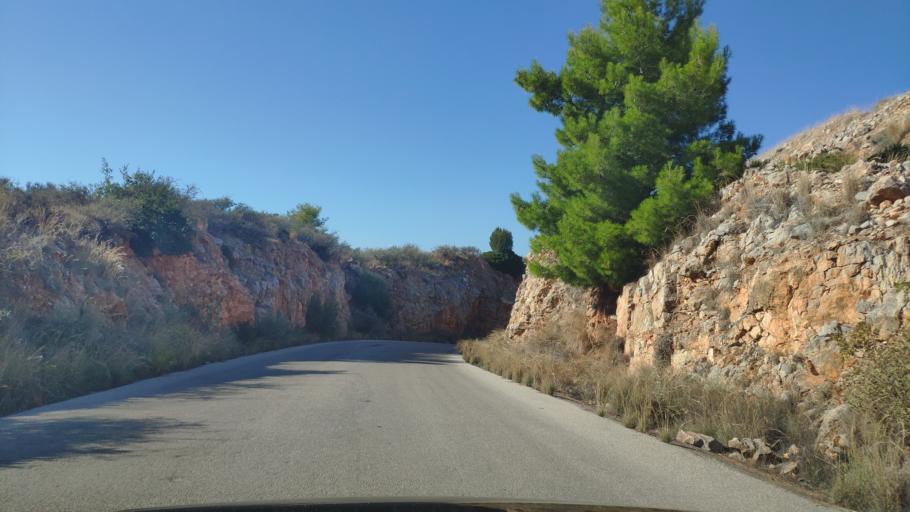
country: GR
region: Attica
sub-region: Nomos Piraios
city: Galatas
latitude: 37.5674
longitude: 23.3599
